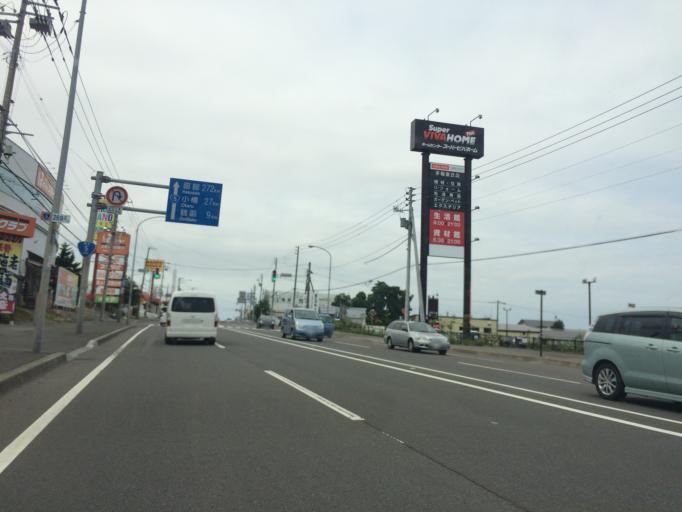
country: JP
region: Hokkaido
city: Sapporo
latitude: 43.1006
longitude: 141.2533
